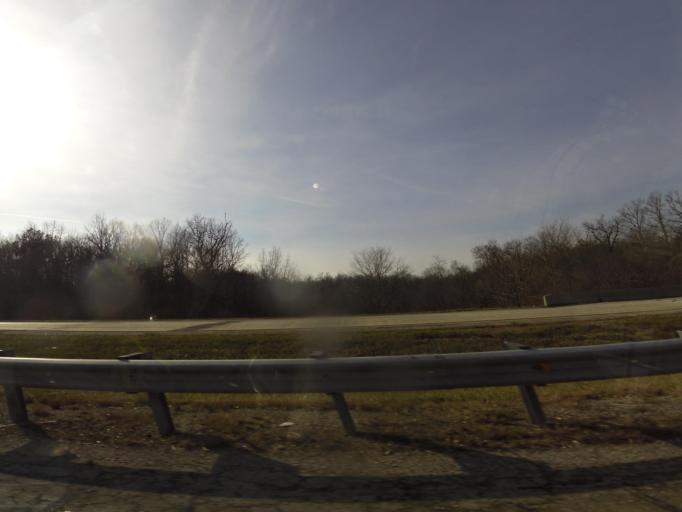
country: US
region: Illinois
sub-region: De Witt County
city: Clinton
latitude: 40.1322
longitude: -88.9701
